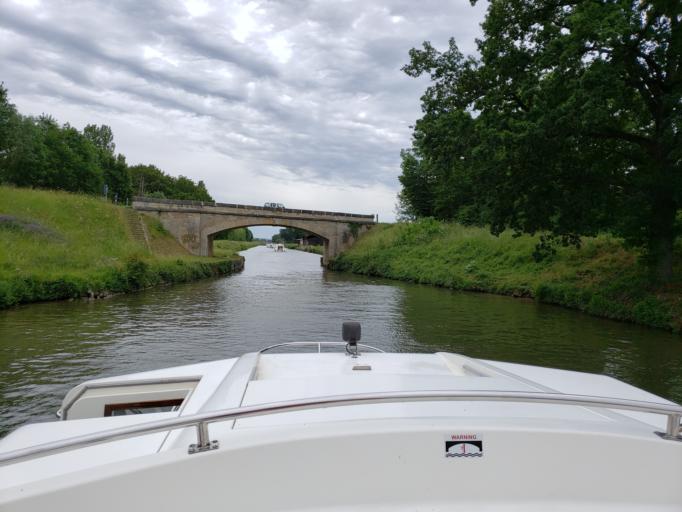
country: FR
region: Bourgogne
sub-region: Departement de l'Yonne
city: Appoigny
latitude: 47.8873
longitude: 3.5434
